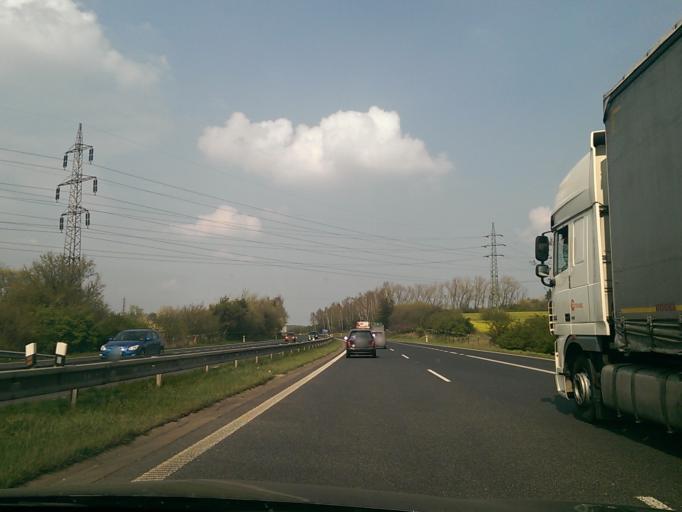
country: CZ
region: Central Bohemia
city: Benatky nad Jizerou
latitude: 50.3223
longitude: 14.8723
